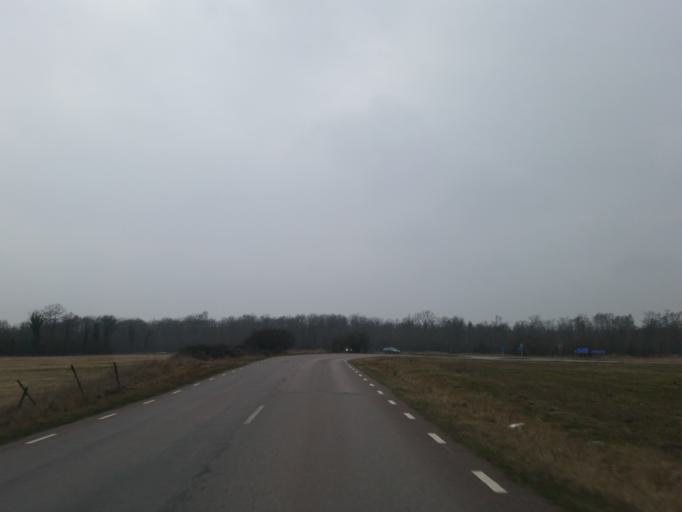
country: SE
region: Kalmar
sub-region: Morbylanga Kommun
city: Sodra Sandby
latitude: 56.6525
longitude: 16.5618
